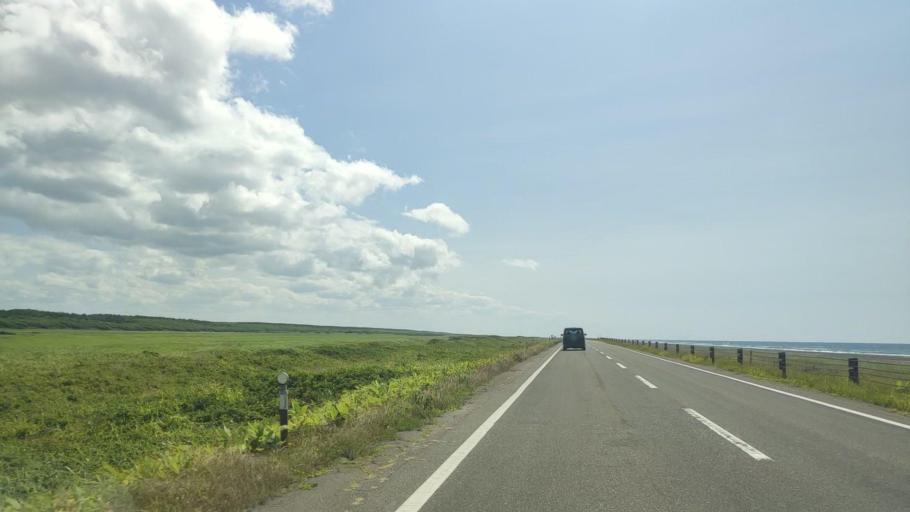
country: JP
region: Hokkaido
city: Wakkanai
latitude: 45.1720
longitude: 141.5811
